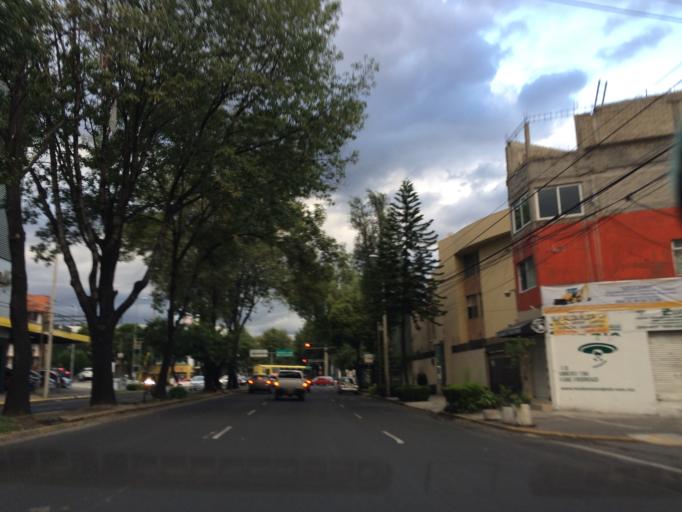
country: MX
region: Mexico City
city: Colonia del Valle
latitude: 19.3686
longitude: -99.1608
